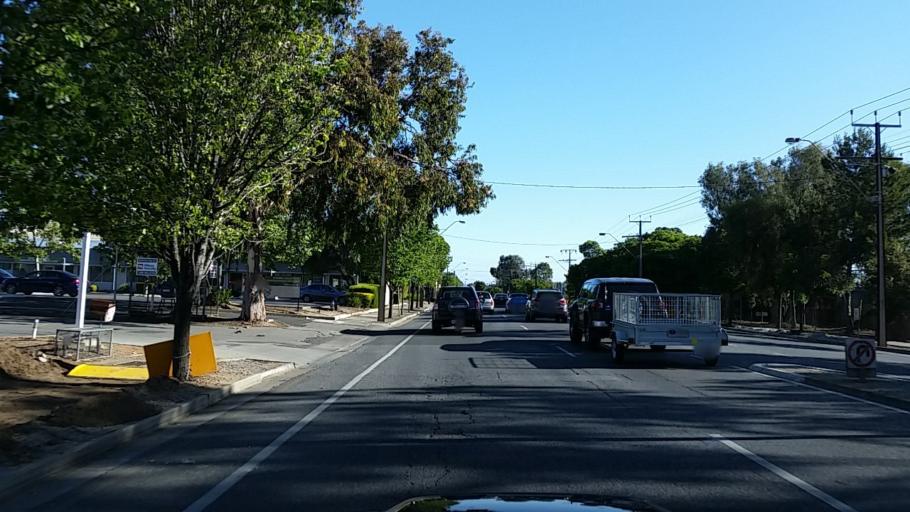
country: AU
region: South Australia
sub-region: City of West Torrens
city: Plympton
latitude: -34.9444
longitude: 138.5534
